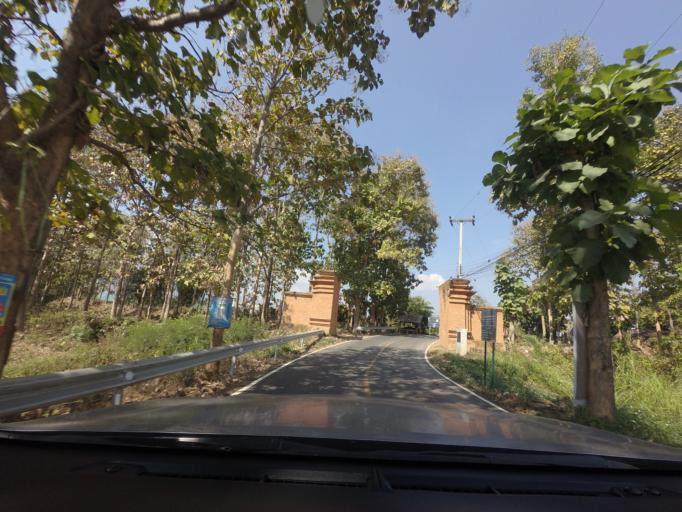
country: TH
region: Mae Hong Son
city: Wiang Nuea
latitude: 19.3746
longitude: 98.4455
